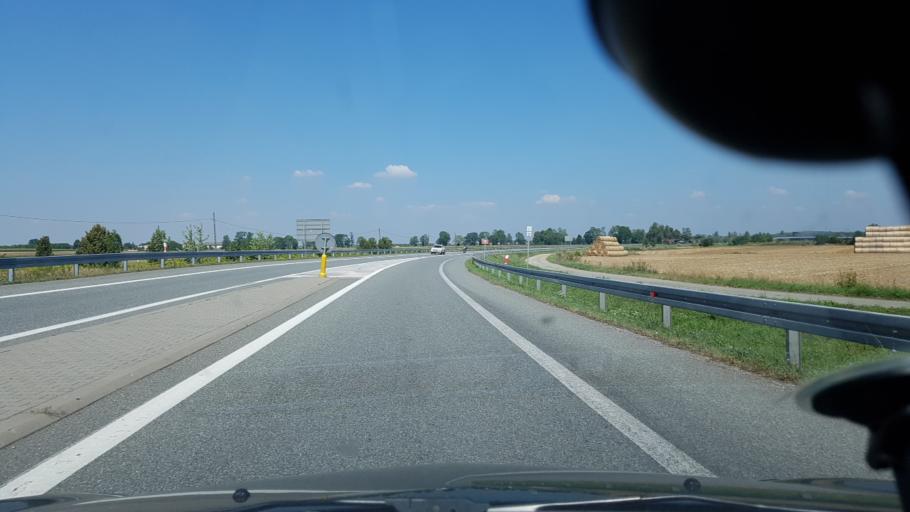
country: PL
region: Silesian Voivodeship
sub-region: Powiat wodzislawski
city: Olza
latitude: 49.9429
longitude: 18.3273
